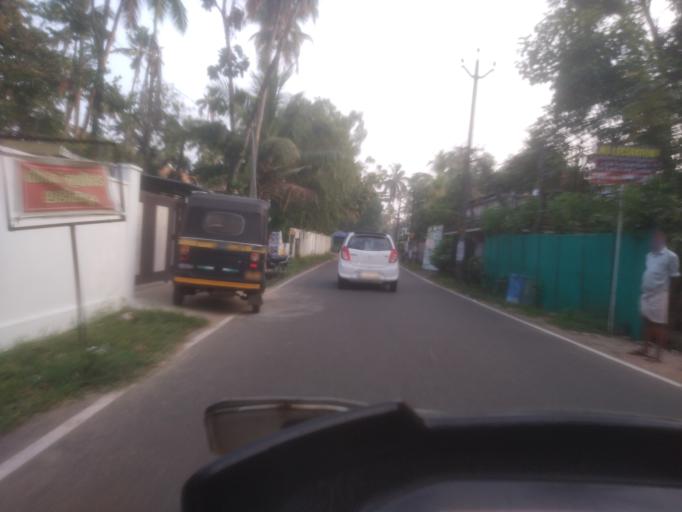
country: IN
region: Kerala
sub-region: Ernakulam
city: Cochin
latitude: 10.0063
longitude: 76.2199
